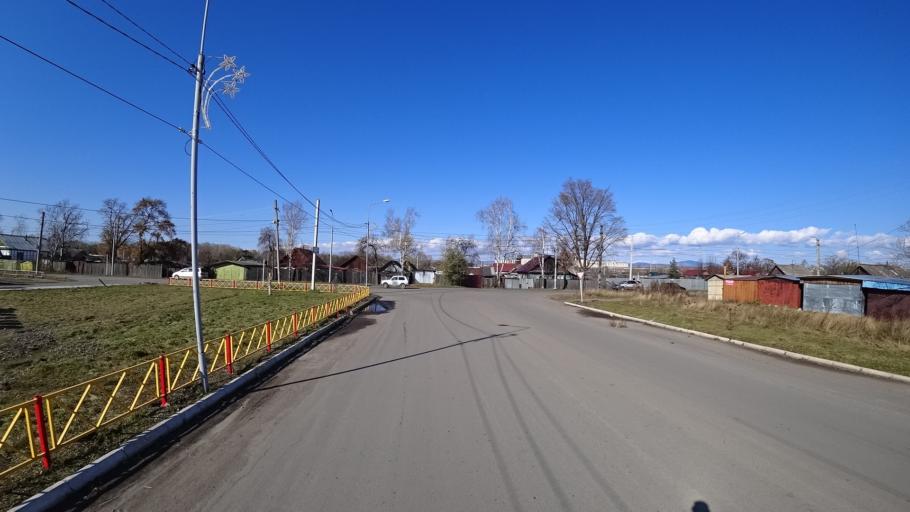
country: RU
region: Khabarovsk Krai
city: Amursk
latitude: 50.1011
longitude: 136.5107
